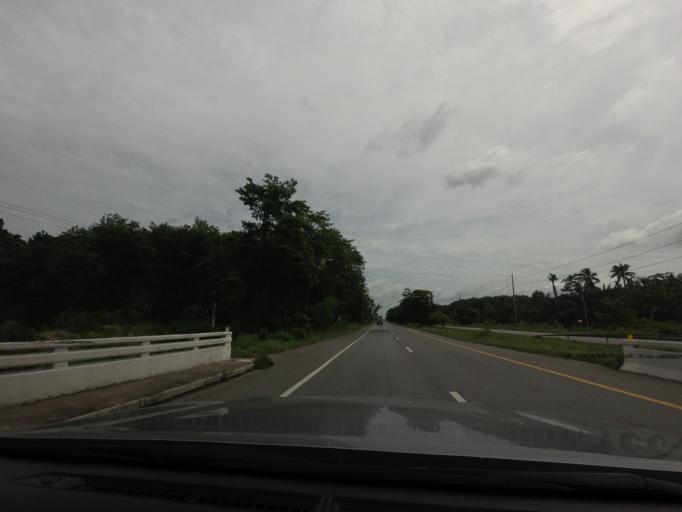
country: TH
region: Surat Thani
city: Phrasaeng
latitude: 8.5311
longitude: 99.3462
